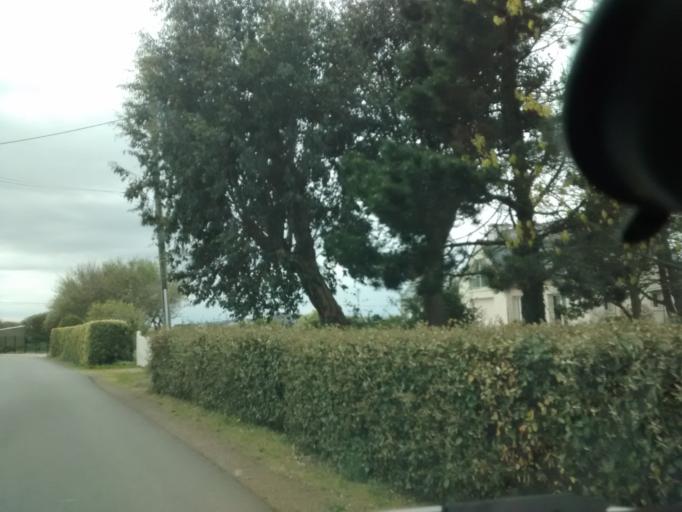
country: FR
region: Brittany
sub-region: Departement des Cotes-d'Armor
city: Ploubazlanec
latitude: 48.8043
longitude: -3.0198
